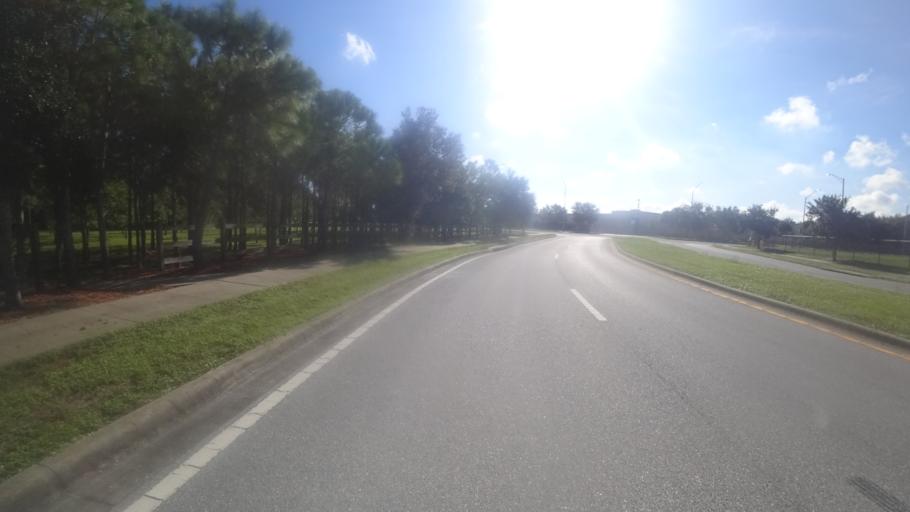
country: US
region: Florida
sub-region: Manatee County
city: Ellenton
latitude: 27.4973
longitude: -82.4841
